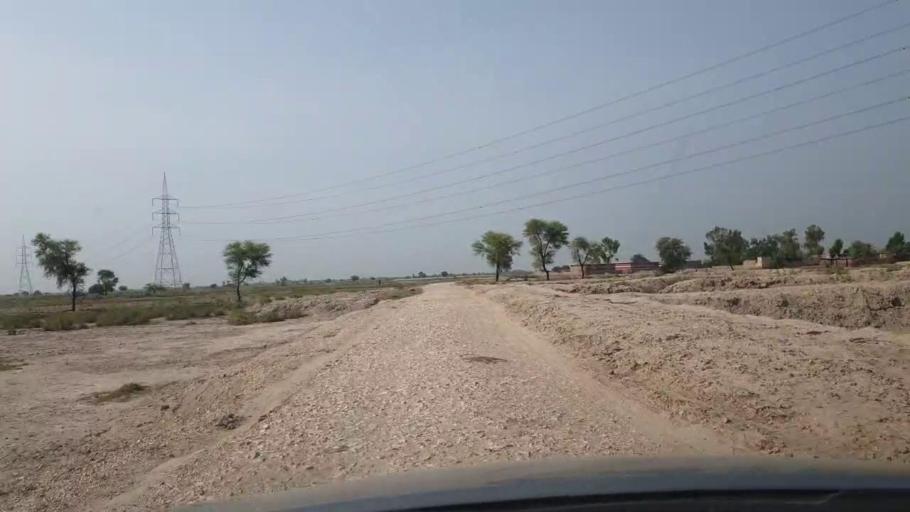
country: PK
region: Sindh
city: Lakhi
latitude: 27.8282
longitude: 68.6965
